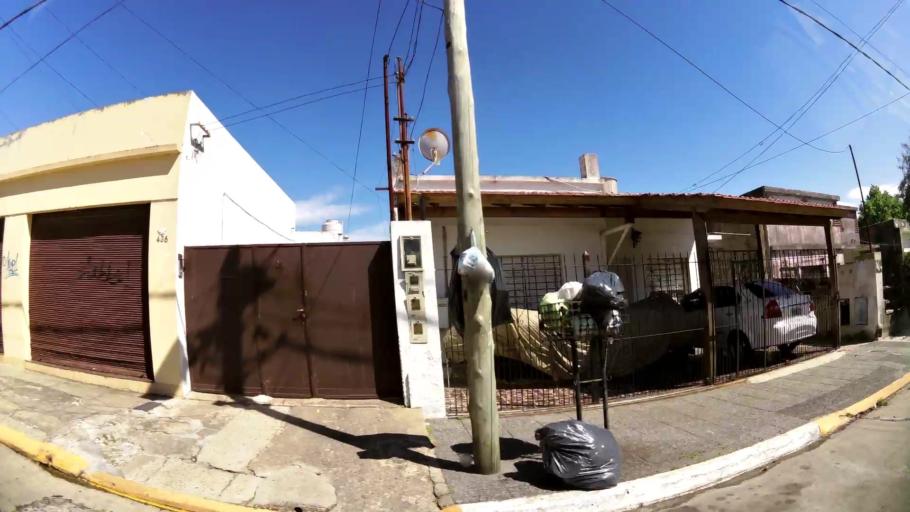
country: AR
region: Buenos Aires
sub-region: Partido de Quilmes
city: Quilmes
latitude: -34.7018
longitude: -58.2852
